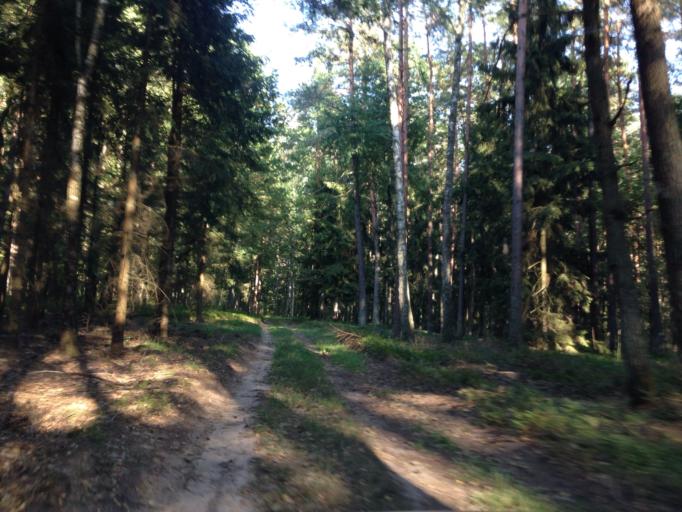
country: PL
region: Kujawsko-Pomorskie
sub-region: Powiat brodnicki
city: Gorzno
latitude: 53.1943
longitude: 19.7250
